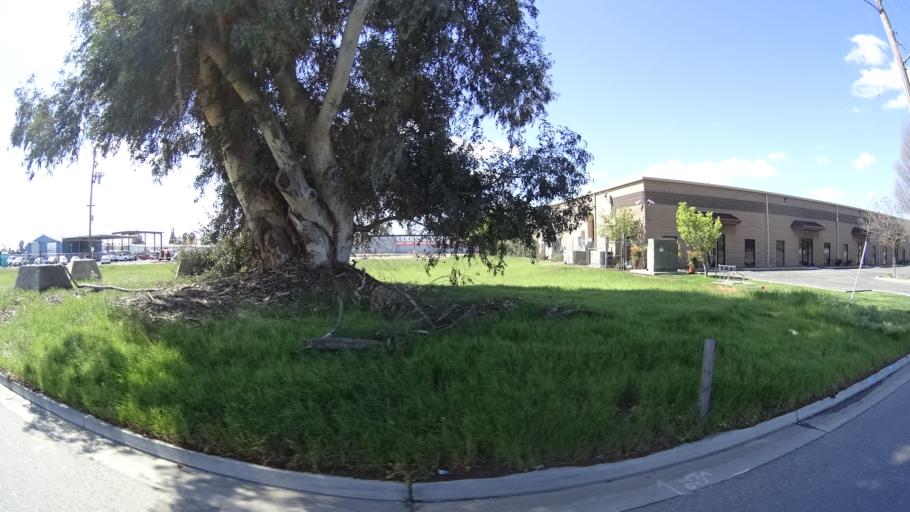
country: US
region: California
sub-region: Fresno County
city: West Park
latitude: 36.8160
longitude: -119.8887
